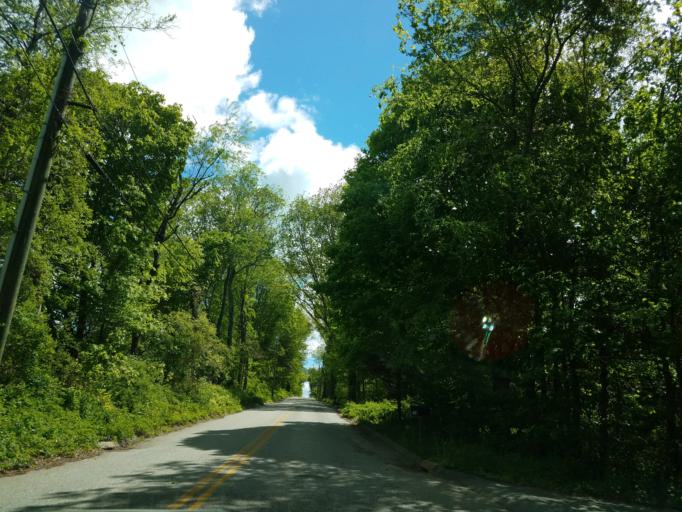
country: US
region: Connecticut
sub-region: New London County
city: Colchester
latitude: 41.5124
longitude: -72.3194
